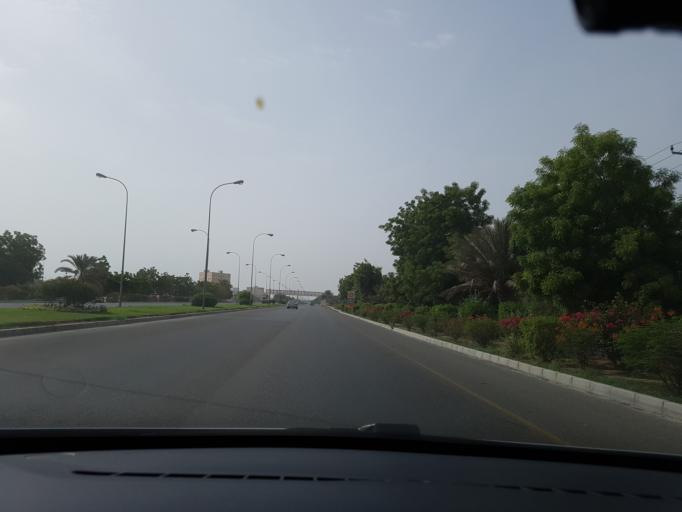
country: OM
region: Al Batinah
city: Al Sohar
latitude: 24.3629
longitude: 56.7084
